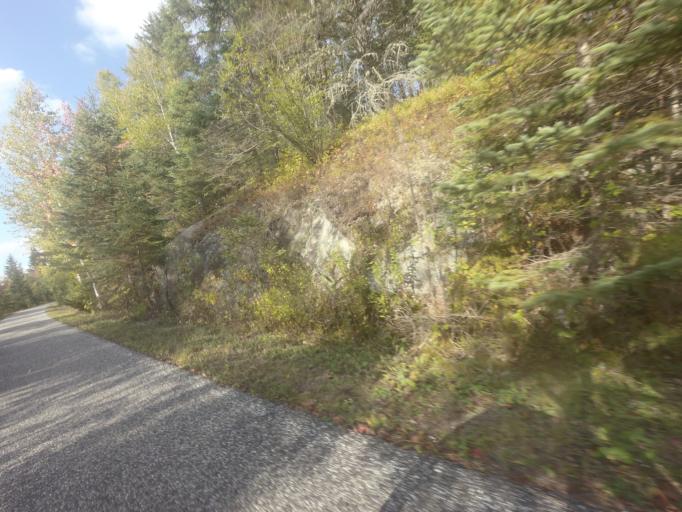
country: CA
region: Quebec
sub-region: Laurentides
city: Labelle
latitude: 46.3257
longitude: -74.7858
